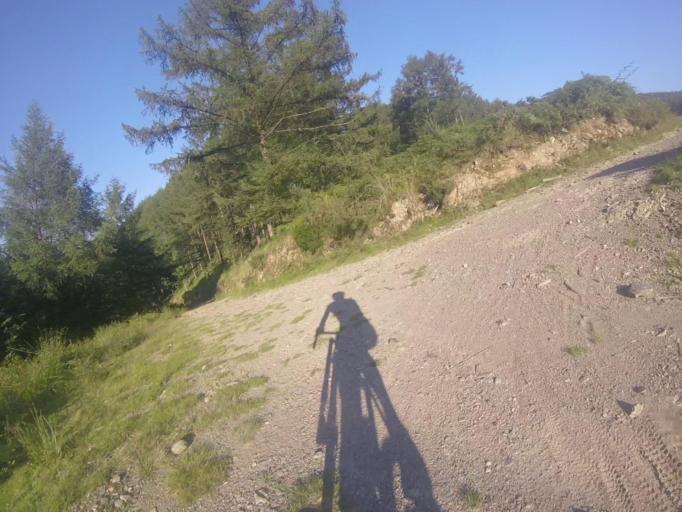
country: ES
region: Navarre
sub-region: Provincia de Navarra
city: Arano
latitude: 43.2504
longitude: -1.8542
